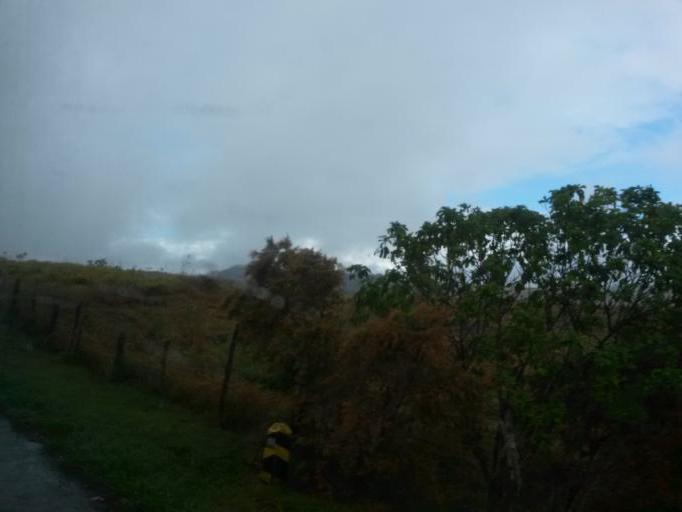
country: CO
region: Cauca
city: El Bordo
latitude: 2.1511
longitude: -76.9171
